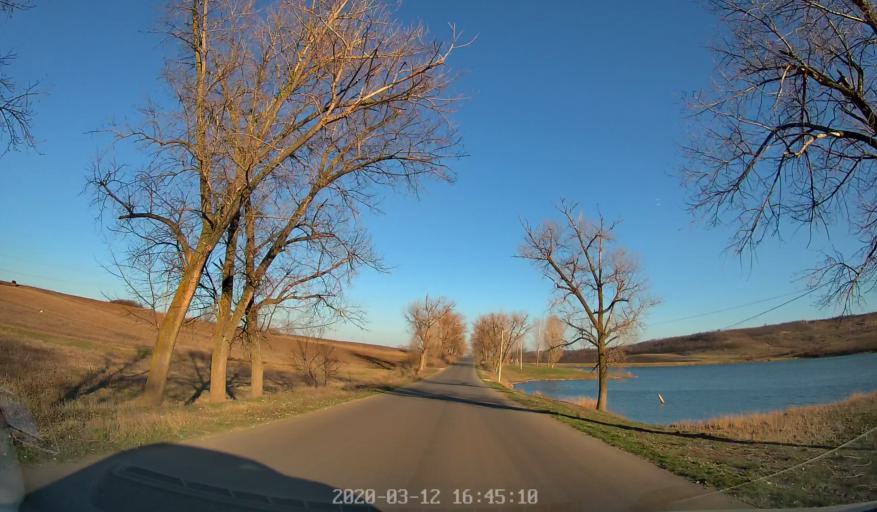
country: MD
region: Anenii Noi
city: Anenii Noi
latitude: 46.8151
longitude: 29.1657
